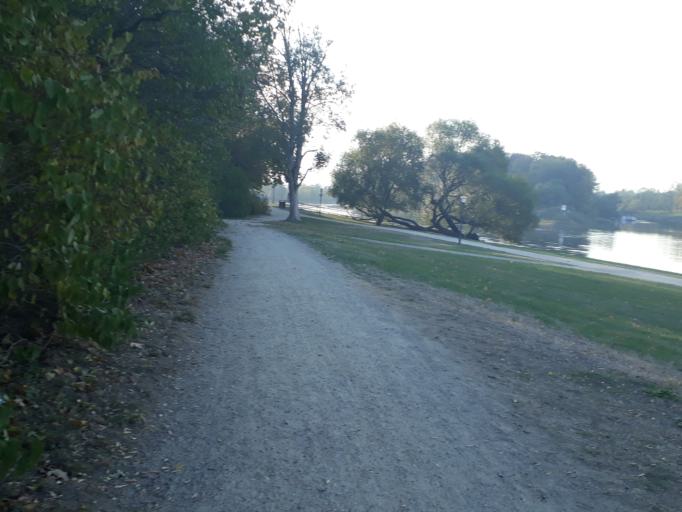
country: DE
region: Saxony
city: Heidenau
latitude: 51.0105
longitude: 13.8654
